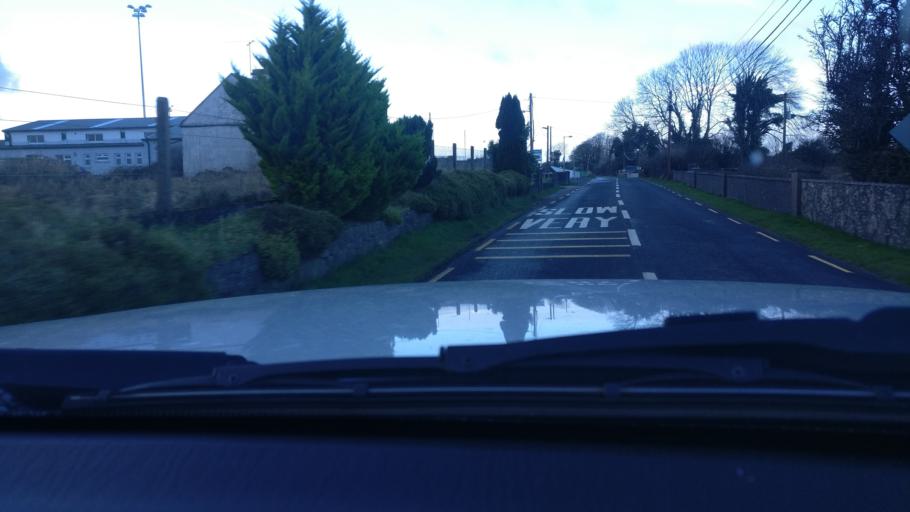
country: IE
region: Connaught
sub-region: County Galway
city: Loughrea
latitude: 53.2237
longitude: -8.3955
